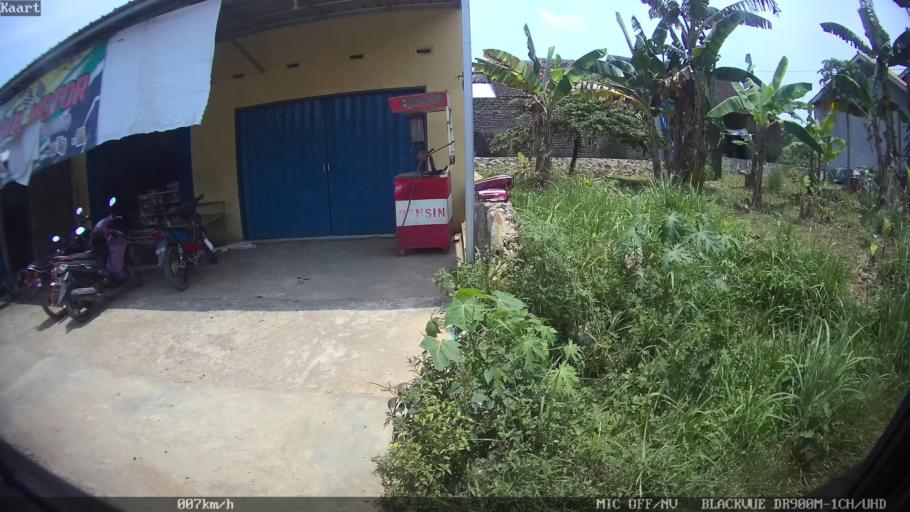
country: ID
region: Lampung
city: Natar
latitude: -5.3243
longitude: 105.2500
